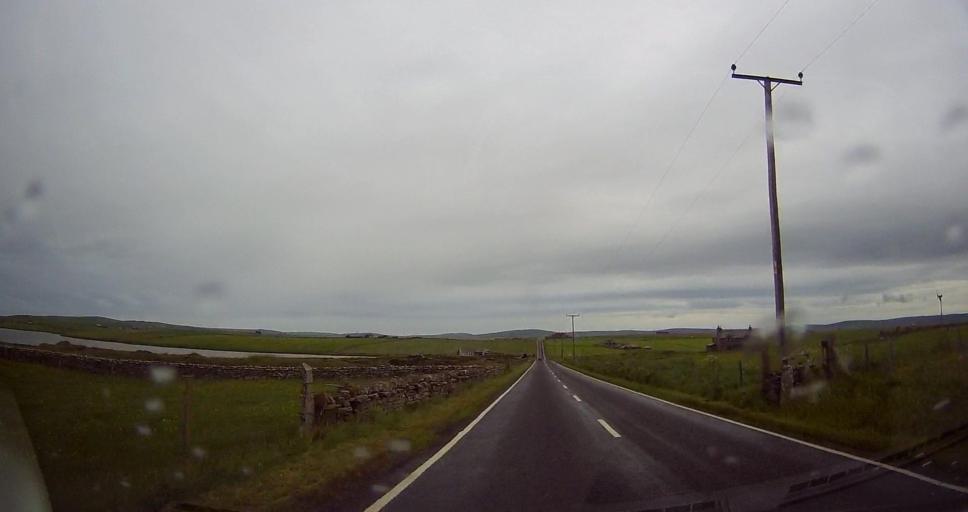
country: GB
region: Scotland
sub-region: Orkney Islands
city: Stromness
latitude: 59.0234
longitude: -3.2962
